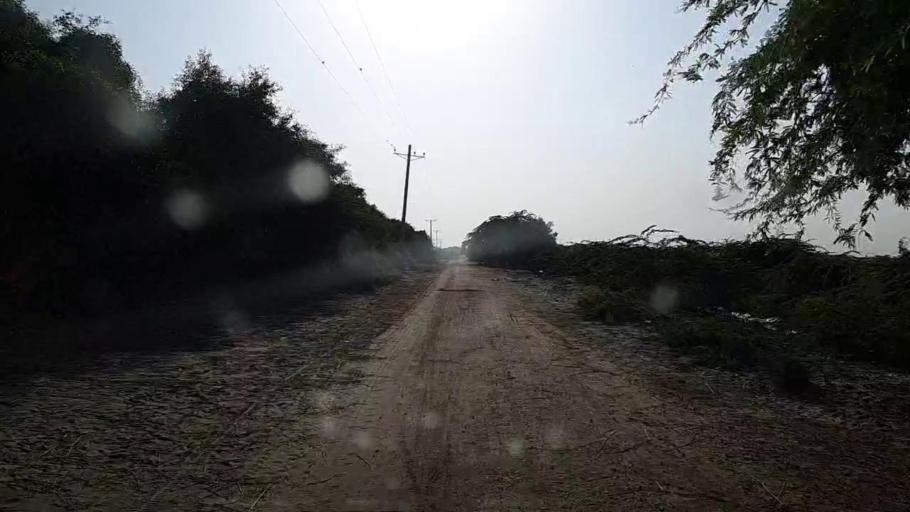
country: PK
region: Sindh
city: Bulri
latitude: 24.7680
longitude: 68.4298
